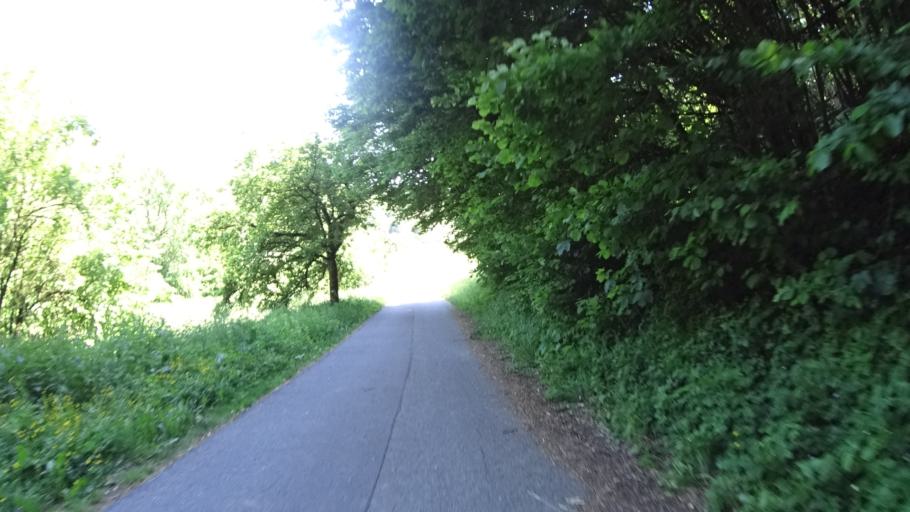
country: DE
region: Bavaria
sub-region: Regierungsbezirk Mittelfranken
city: Adelshofen
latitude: 49.4217
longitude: 10.1465
